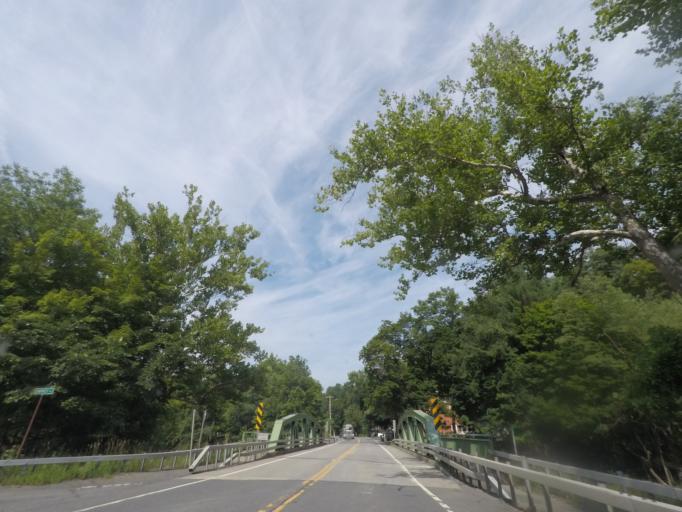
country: US
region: New York
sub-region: Rensselaer County
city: Wynantskill
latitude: 42.7328
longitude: -73.6310
